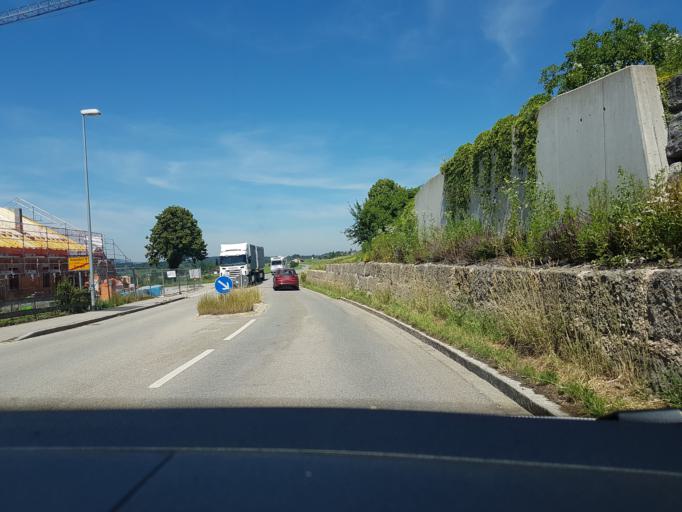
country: DE
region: Bavaria
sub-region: Upper Bavaria
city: Anger
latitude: 47.8390
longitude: 12.8913
